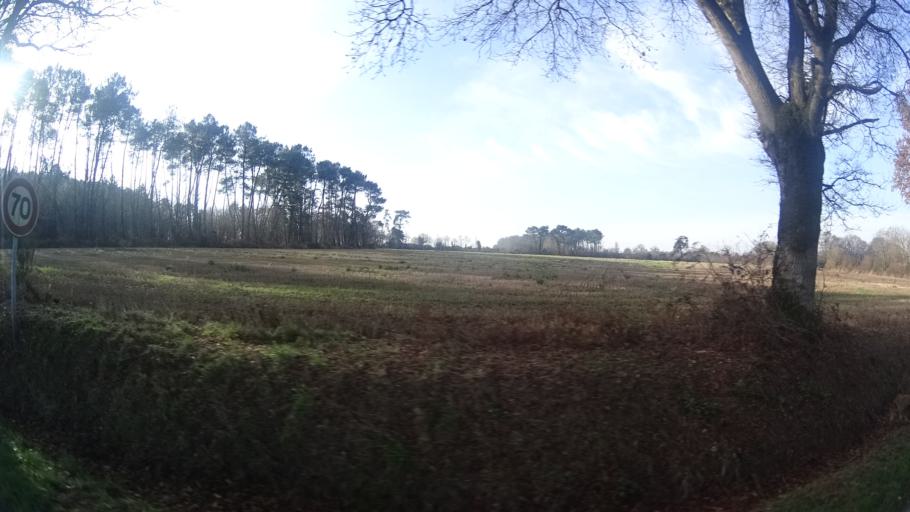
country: FR
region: Brittany
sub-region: Departement du Morbihan
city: Allaire
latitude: 47.6215
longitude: -2.1552
